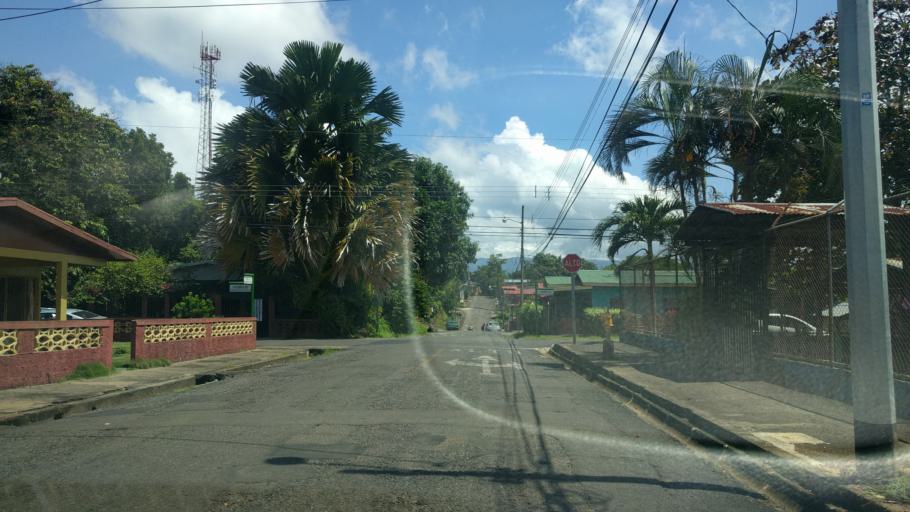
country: CR
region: Puntarenas
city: Esparza
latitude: 9.9910
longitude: -84.6639
